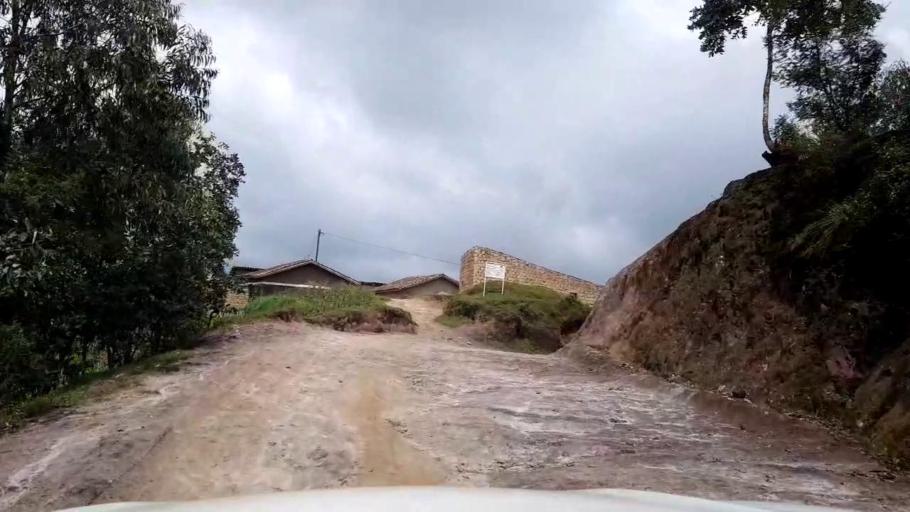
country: RW
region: Western Province
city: Kibuye
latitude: -1.9360
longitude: 29.4559
